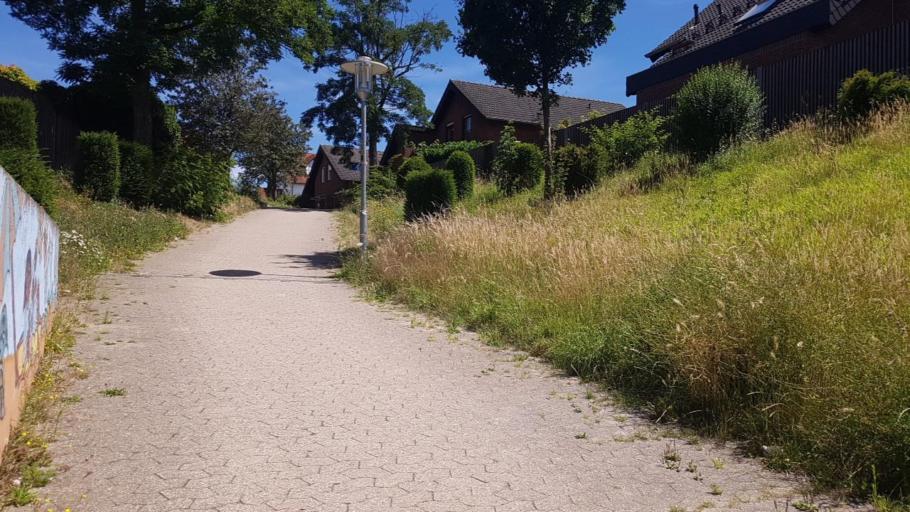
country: DE
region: North Rhine-Westphalia
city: Meckenheim
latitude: 50.6272
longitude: 7.0321
